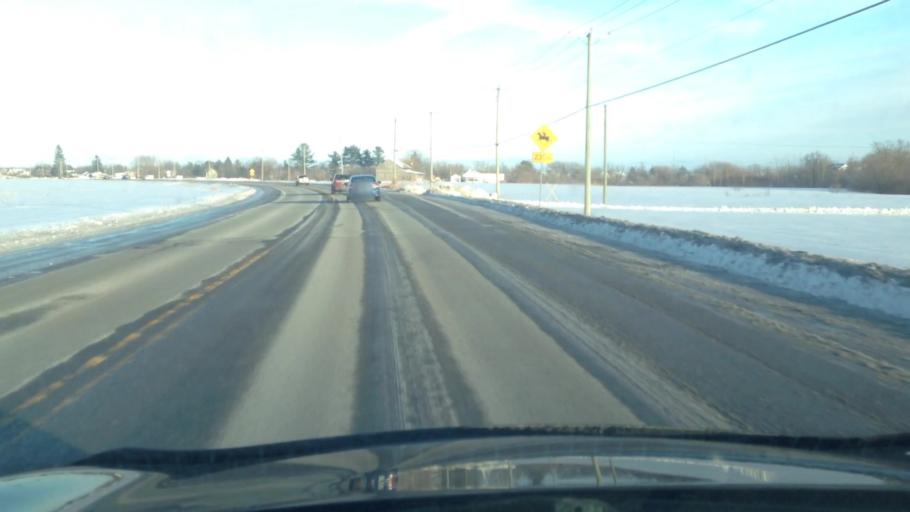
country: CA
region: Quebec
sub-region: Lanaudiere
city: Saint-Lin-Laurentides
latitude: 45.8450
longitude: -73.7953
